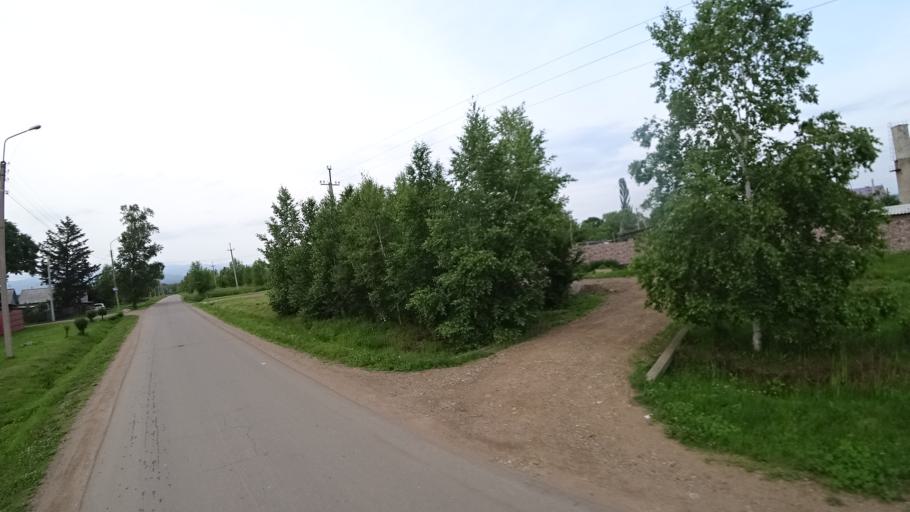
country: RU
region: Primorskiy
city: Novosysoyevka
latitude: 44.2333
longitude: 133.3598
